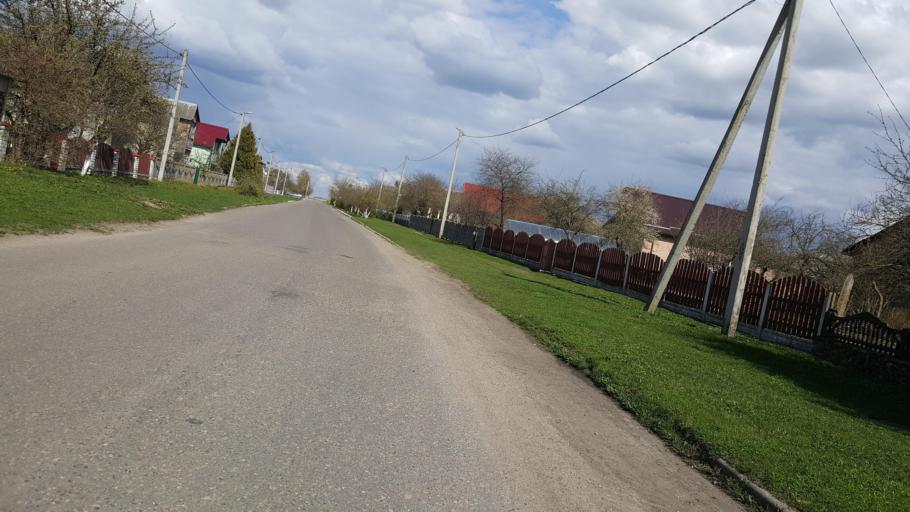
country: BY
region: Brest
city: Kamyanyets
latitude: 52.4080
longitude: 23.6348
